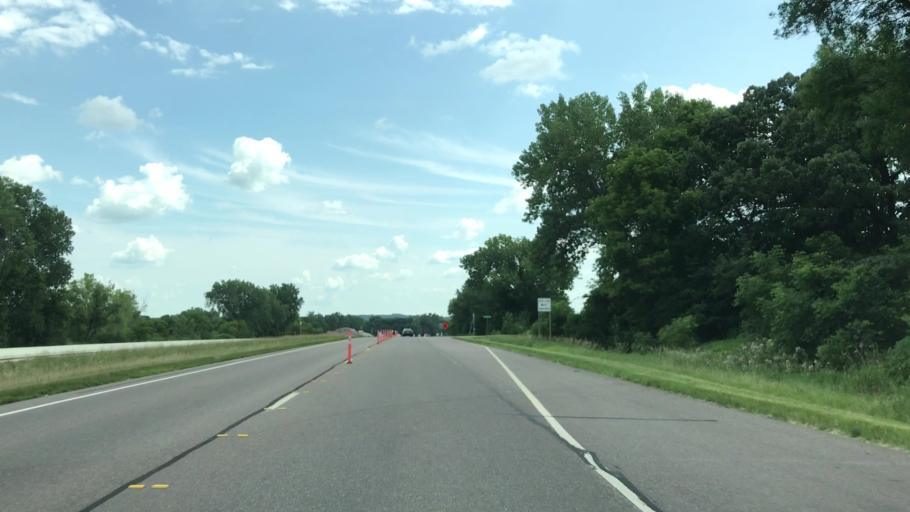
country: US
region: Minnesota
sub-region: Nicollet County
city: Saint Peter
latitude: 44.3551
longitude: -93.9553
